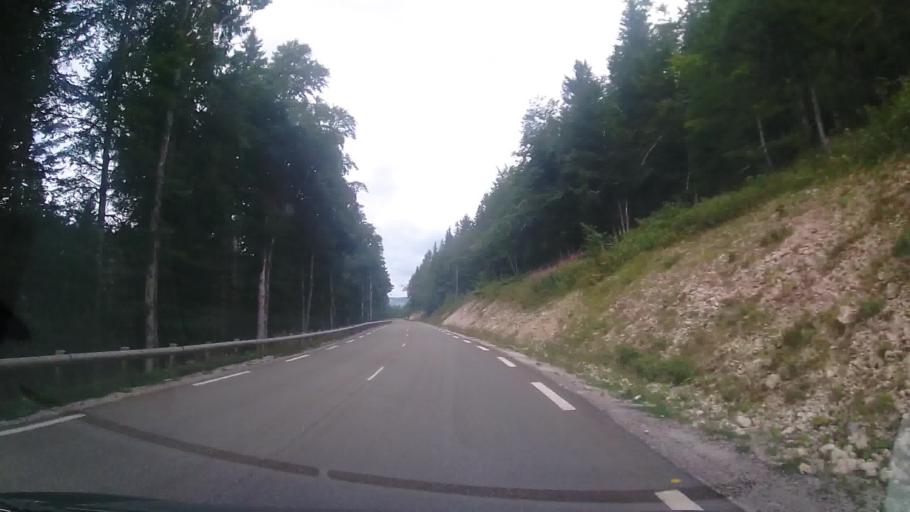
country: FR
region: Franche-Comte
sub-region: Departement du Jura
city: Les Rousses
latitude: 46.4250
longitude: 6.0687
